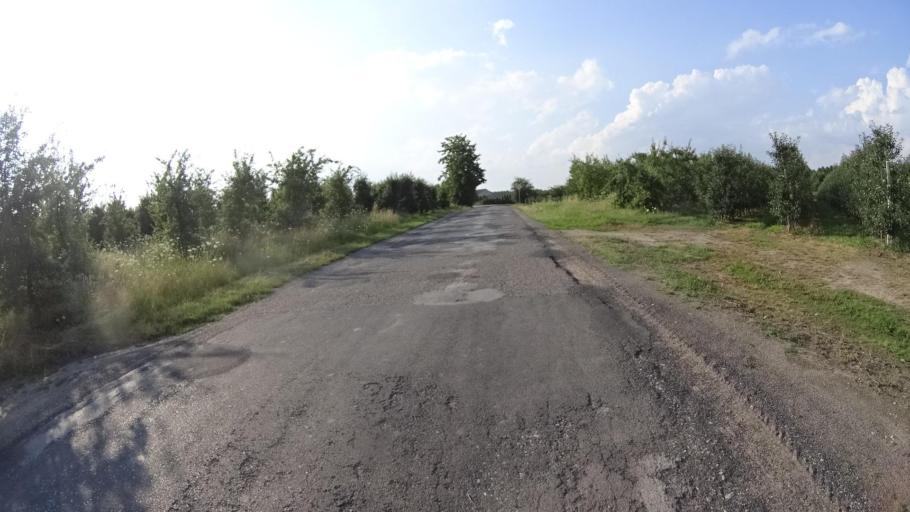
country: PL
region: Masovian Voivodeship
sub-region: Powiat grojecki
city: Goszczyn
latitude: 51.7108
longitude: 20.7912
